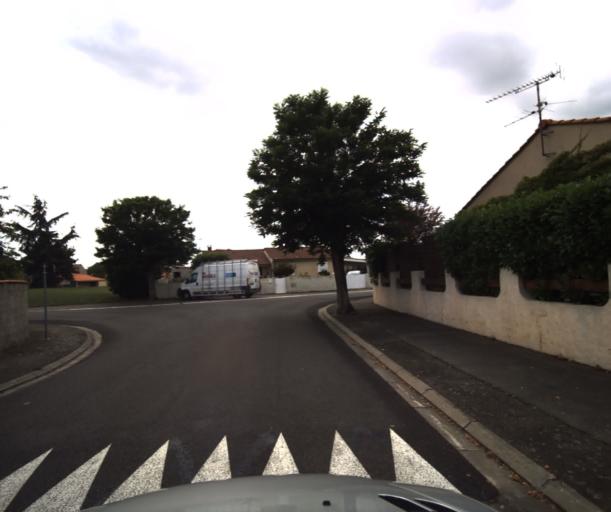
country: FR
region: Midi-Pyrenees
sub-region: Departement de la Haute-Garonne
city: Labarthe-sur-Leze
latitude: 43.4499
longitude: 1.3970
